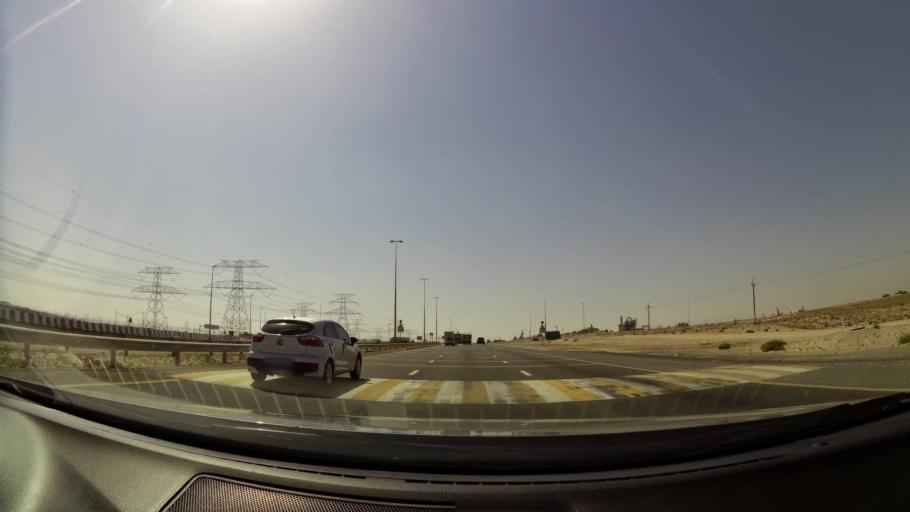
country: AE
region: Dubai
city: Dubai
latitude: 24.9381
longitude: 55.0743
